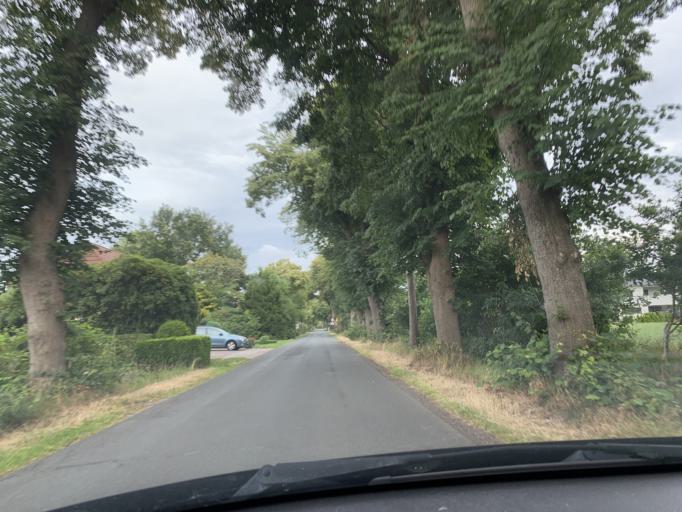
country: DE
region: Lower Saxony
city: Westerstede
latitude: 53.2560
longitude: 7.8969
